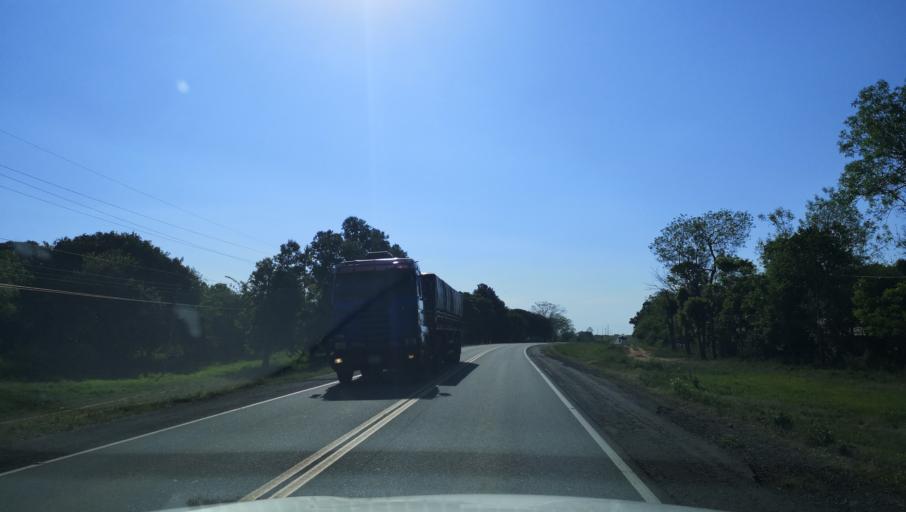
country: PY
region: Misiones
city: Santa Rosa
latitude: -26.8884
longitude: -56.9420
